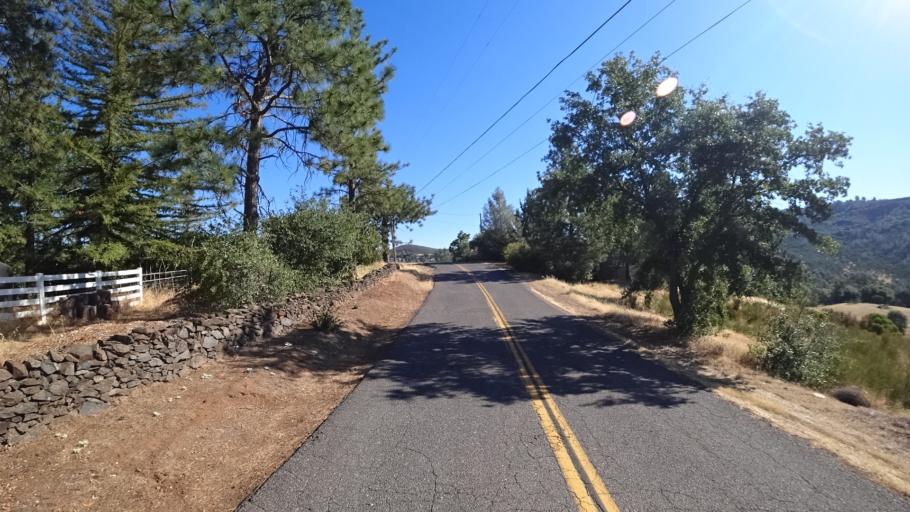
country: US
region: California
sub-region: Calaveras County
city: Murphys
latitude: 38.0772
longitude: -120.4616
